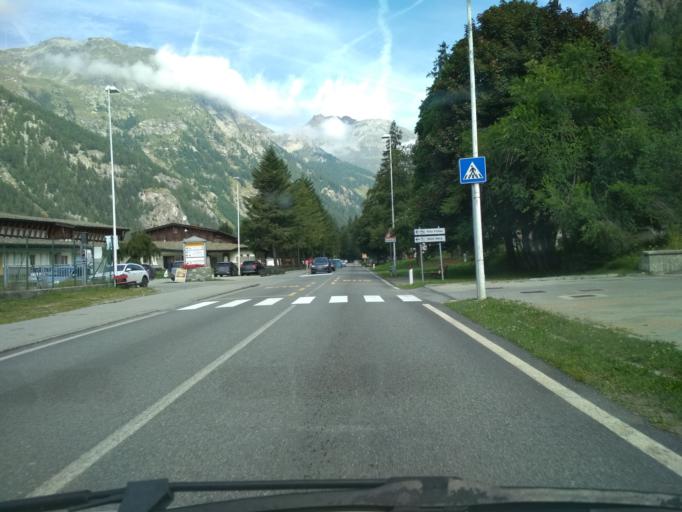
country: IT
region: Aosta Valley
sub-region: Valle d'Aosta
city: Gressoney-Saint-Jean
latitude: 45.7666
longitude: 7.8351
